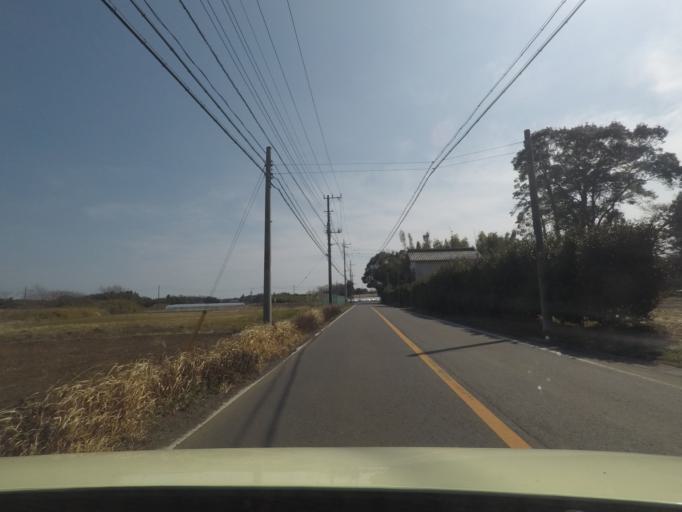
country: JP
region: Ibaraki
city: Okunoya
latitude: 36.2073
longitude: 140.4217
